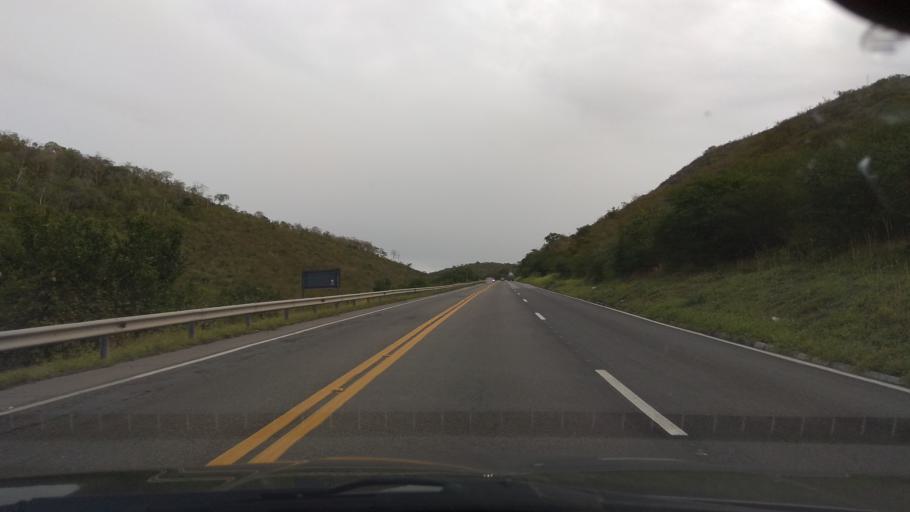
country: BR
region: Bahia
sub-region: Amargosa
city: Amargosa
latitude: -12.8902
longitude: -39.8589
